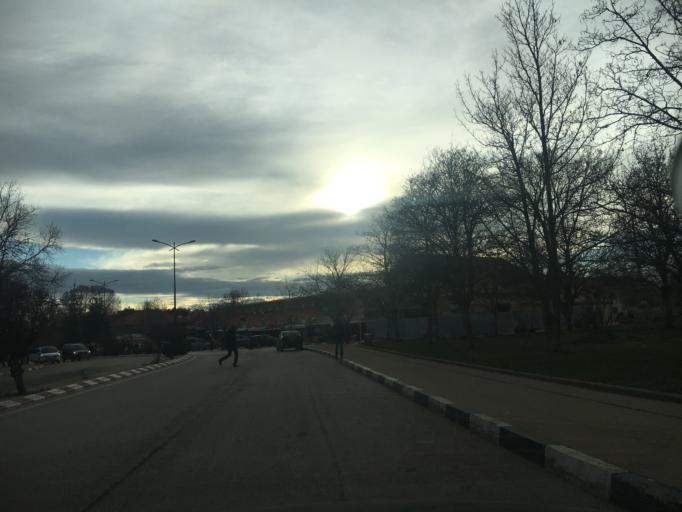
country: MA
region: Meknes-Tafilalet
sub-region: Ifrane
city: Ifrane
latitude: 33.5265
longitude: -5.1142
